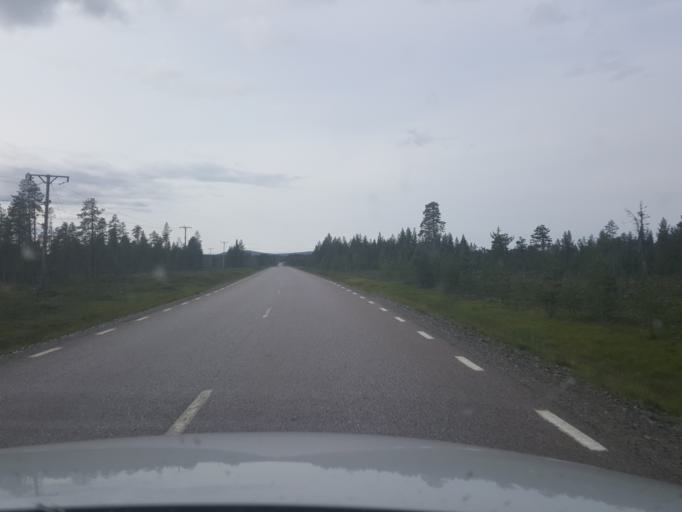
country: SE
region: Norrbotten
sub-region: Arjeplogs Kommun
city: Arjeplog
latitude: 65.7182
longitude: 18.0812
